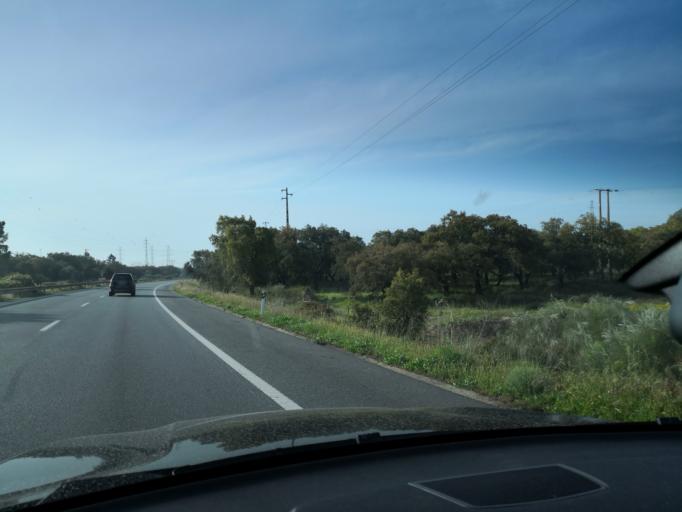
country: PT
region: Setubal
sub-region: Palmela
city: Palmela
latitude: 38.5790
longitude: -8.8693
